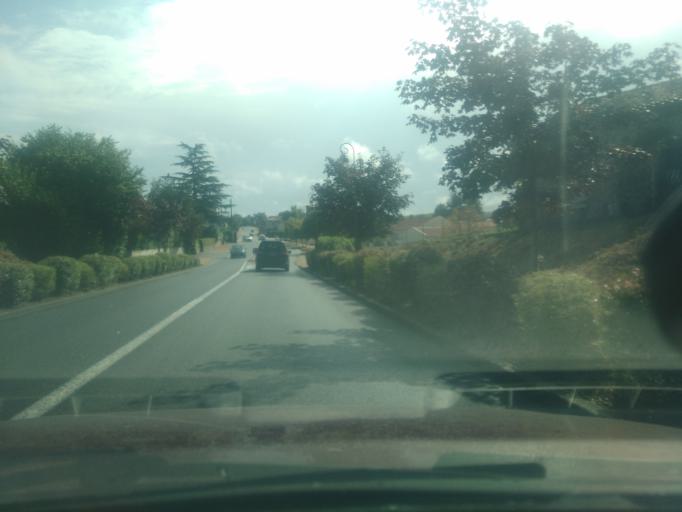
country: FR
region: Poitou-Charentes
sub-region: Departement des Deux-Sevres
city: Le Tallud
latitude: 46.6310
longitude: -0.2966
